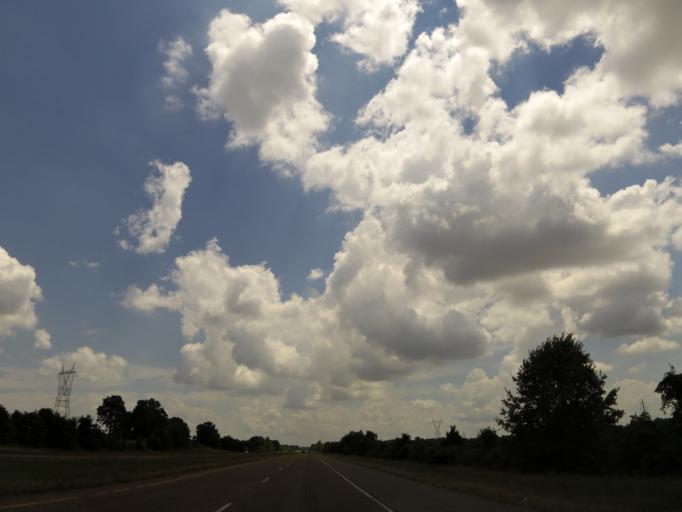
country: US
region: Tennessee
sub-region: Dyer County
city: Dyersburg
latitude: 36.0130
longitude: -89.3413
